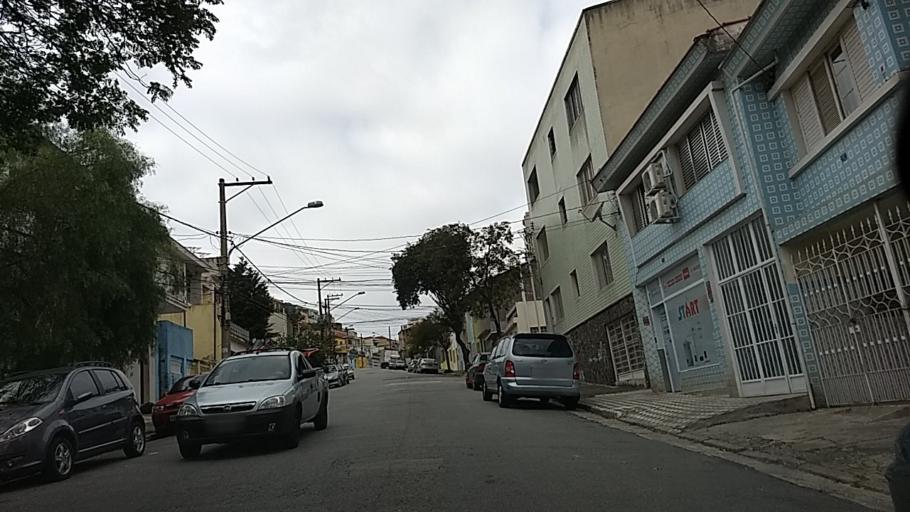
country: BR
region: Sao Paulo
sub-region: Sao Paulo
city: Sao Paulo
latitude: -23.5034
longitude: -46.6086
